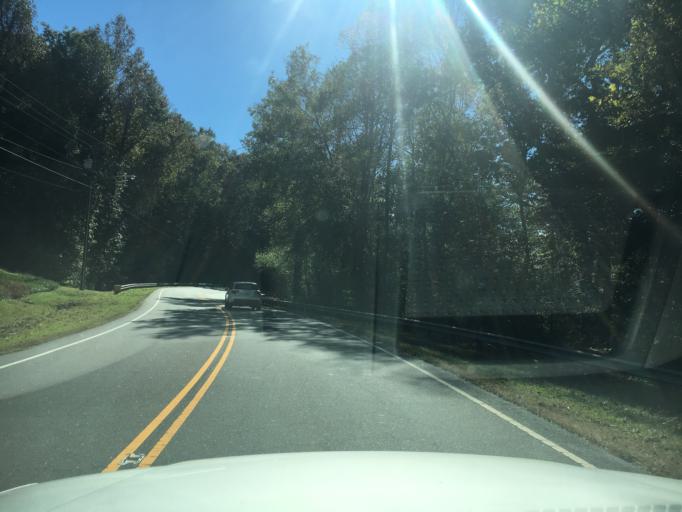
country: US
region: North Carolina
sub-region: Burke County
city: Morganton
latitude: 35.7426
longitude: -81.7092
